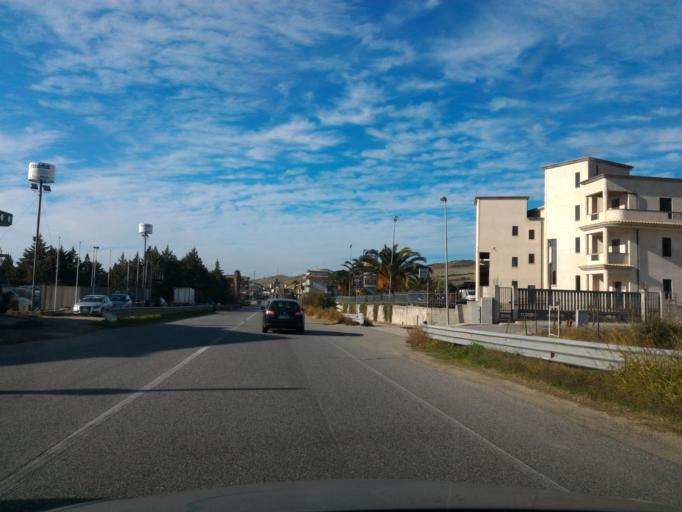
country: IT
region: Calabria
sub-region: Provincia di Catanzaro
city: Cropani Marina
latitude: 38.9255
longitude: 16.8163
